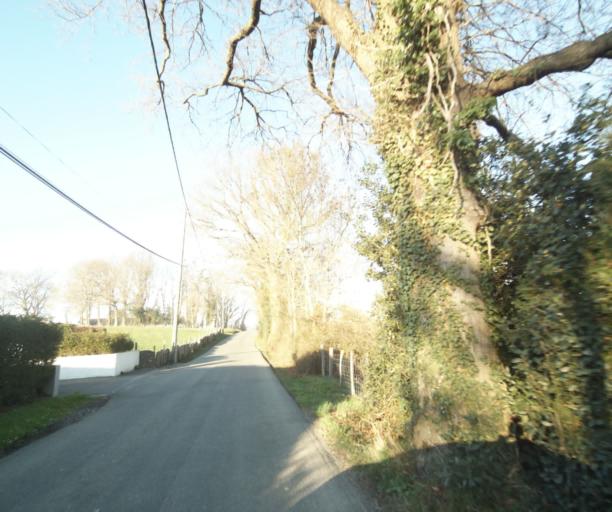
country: FR
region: Aquitaine
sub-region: Departement des Pyrenees-Atlantiques
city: Urrugne
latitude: 43.3432
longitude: -1.6989
